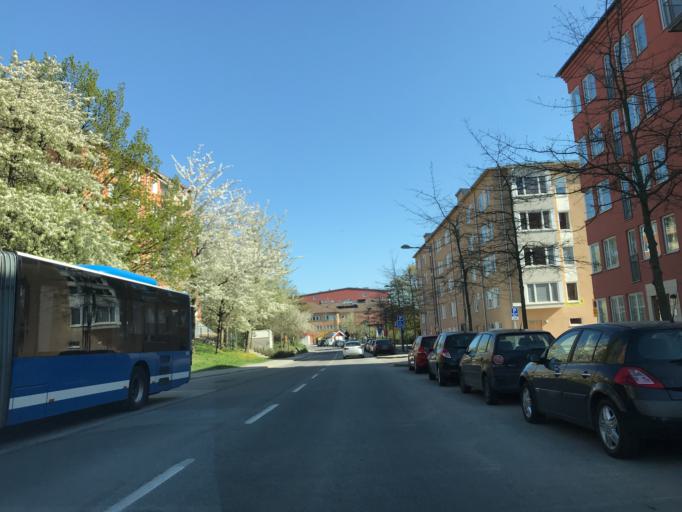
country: SE
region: Stockholm
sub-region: Huddinge Kommun
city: Huddinge
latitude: 59.2803
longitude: 18.0049
